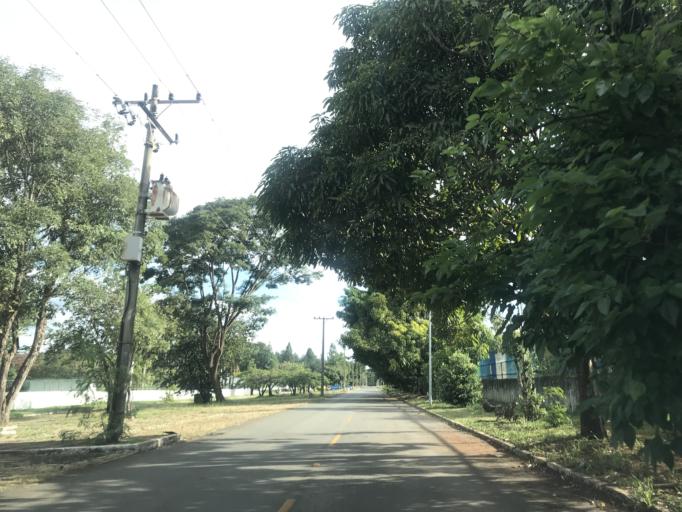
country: BR
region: Federal District
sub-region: Brasilia
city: Brasilia
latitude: -15.8145
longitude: -47.8855
